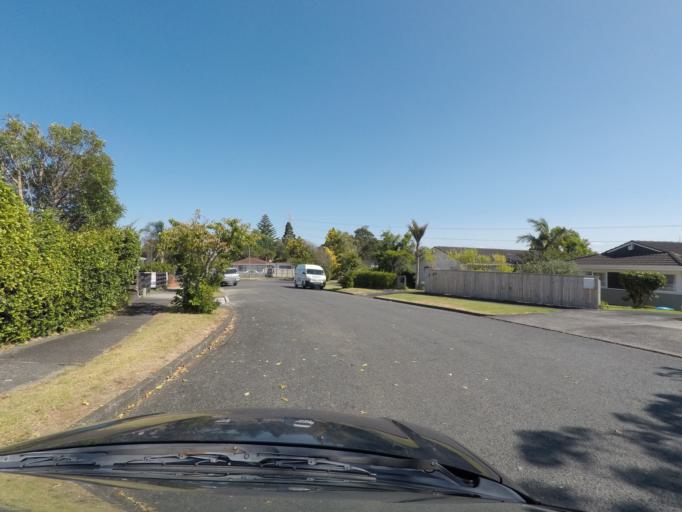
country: NZ
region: Auckland
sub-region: Auckland
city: Rosebank
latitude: -36.8904
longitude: 174.6763
